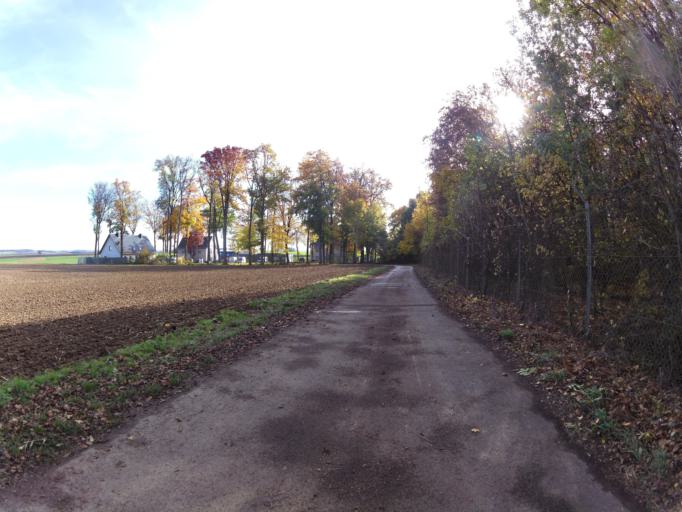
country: DE
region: Bavaria
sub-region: Regierungsbezirk Unterfranken
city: Gaukonigshofen
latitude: 49.6594
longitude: 9.9837
